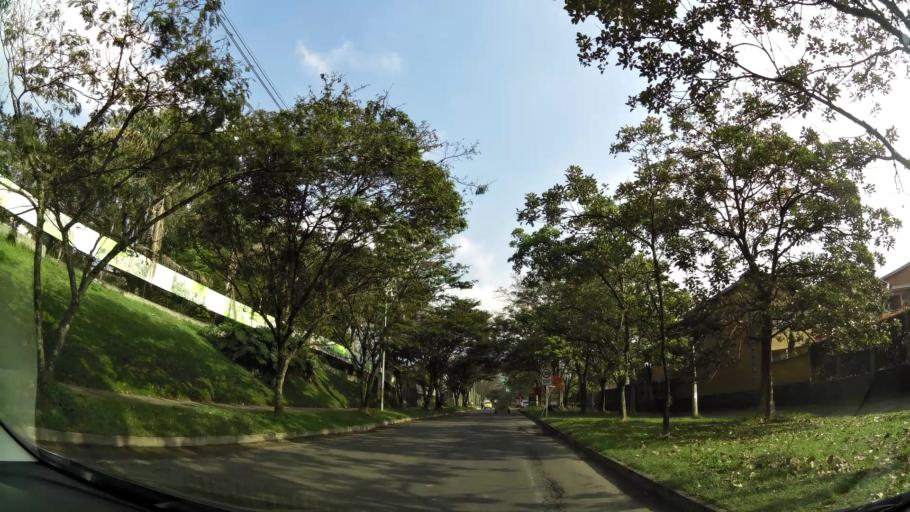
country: CO
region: Antioquia
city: La Estrella
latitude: 6.1617
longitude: -75.6284
